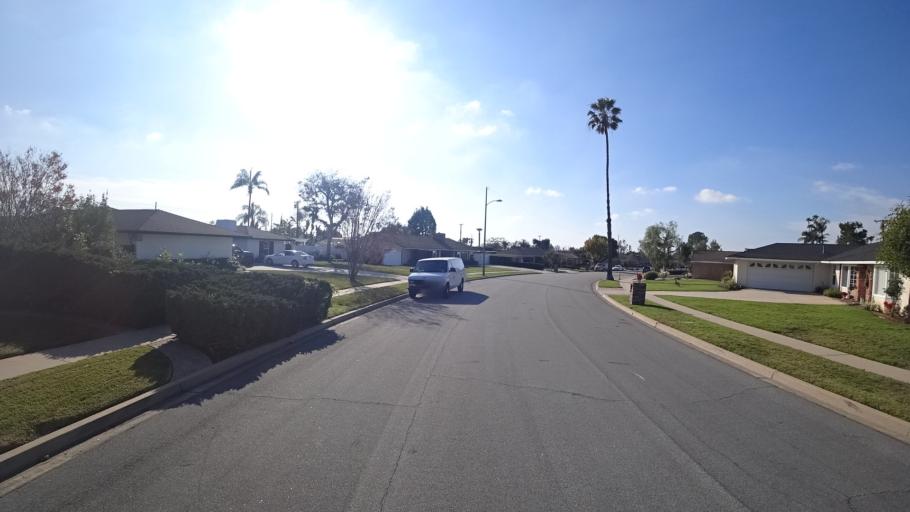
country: US
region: California
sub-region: Orange County
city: North Tustin
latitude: 33.7612
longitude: -117.8083
